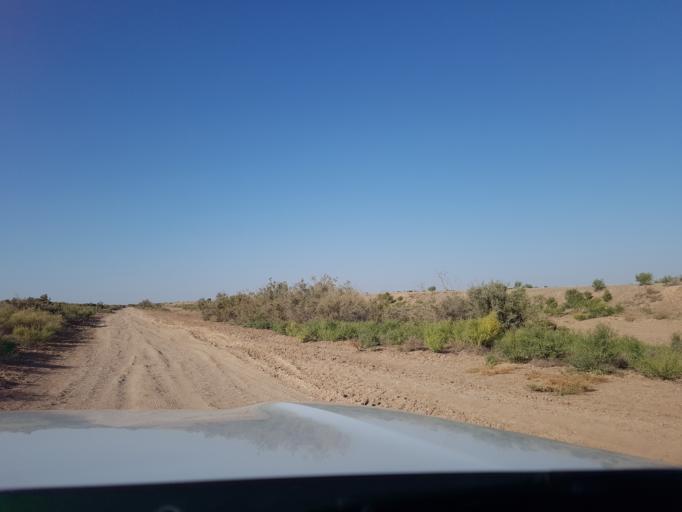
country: IR
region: Razavi Khorasan
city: Sarakhs
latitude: 36.9765
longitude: 61.3850
